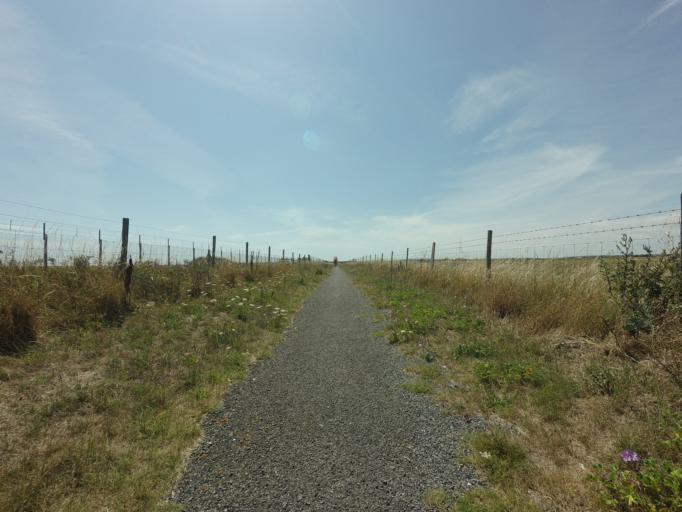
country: GB
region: England
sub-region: Kent
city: Lydd
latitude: 50.9311
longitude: 0.8383
